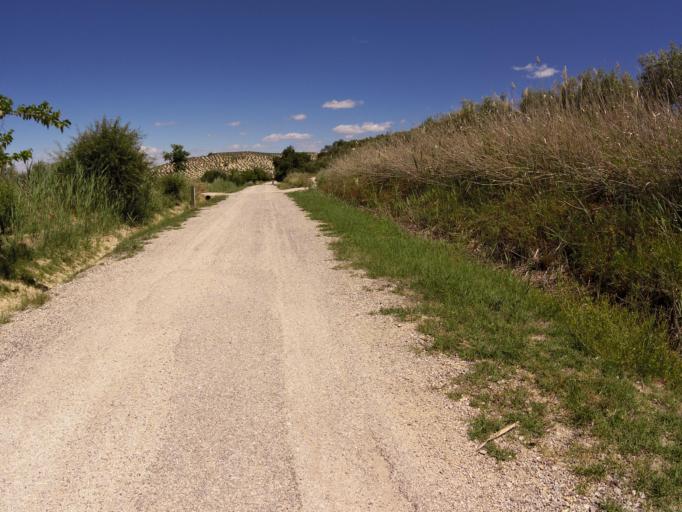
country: ES
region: Andalusia
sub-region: Provincia de Jaen
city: Torredonjimeno
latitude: 37.7710
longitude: -3.9336
